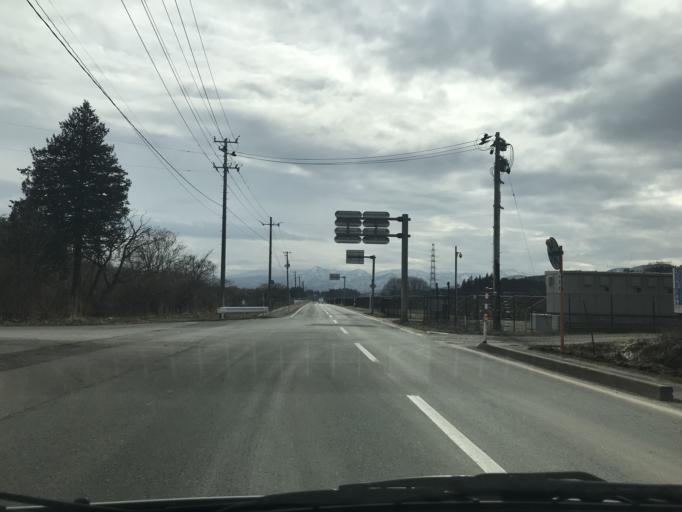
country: JP
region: Iwate
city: Hanamaki
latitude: 39.3690
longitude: 141.0016
